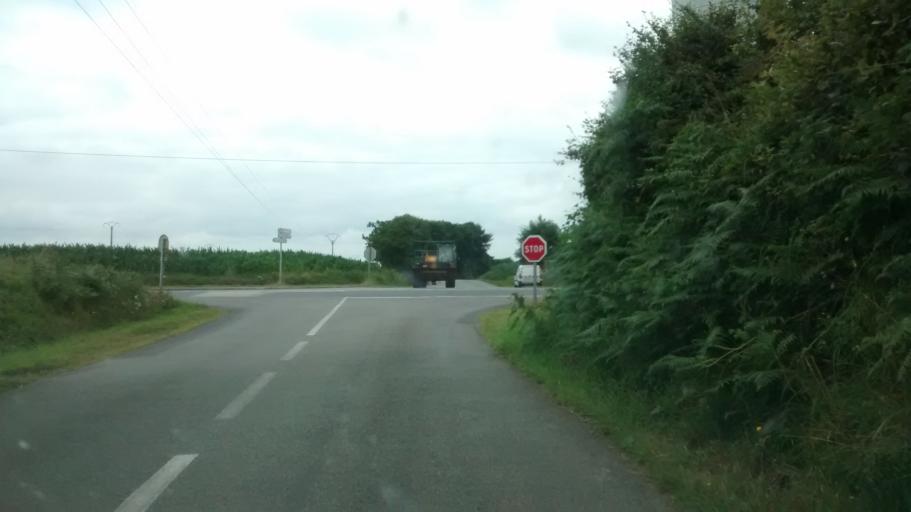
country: FR
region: Brittany
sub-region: Departement du Finistere
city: Plouedern
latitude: 48.4826
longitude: -4.2599
